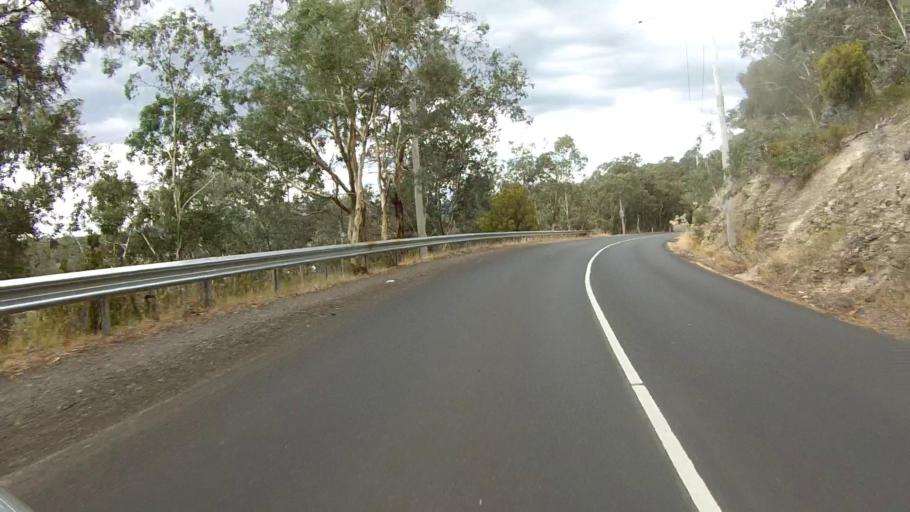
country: AU
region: Tasmania
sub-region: Hobart
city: Dynnyrne
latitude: -42.9011
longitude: 147.2924
